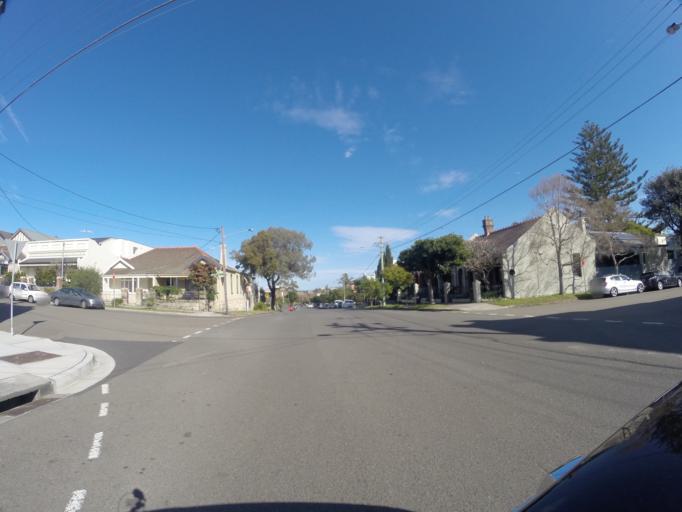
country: AU
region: New South Wales
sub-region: Randwick
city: Clovelly
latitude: -33.9095
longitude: 151.2547
